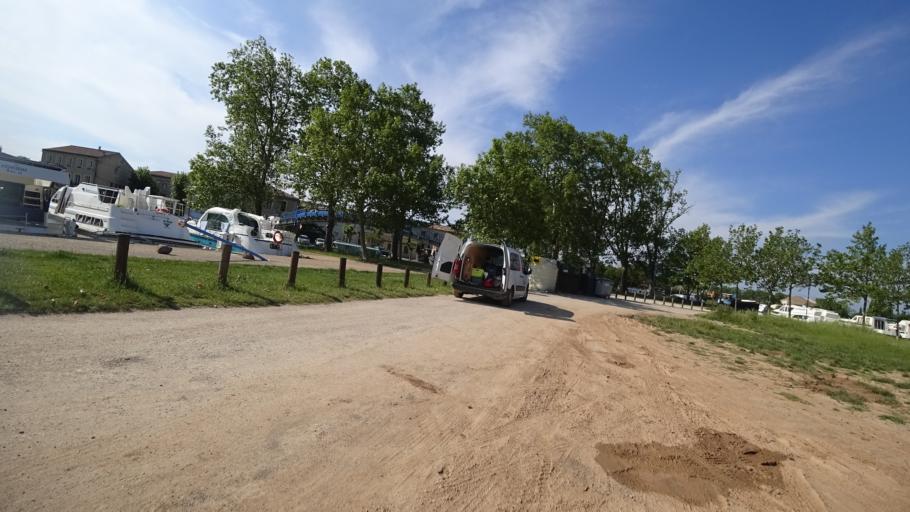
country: FR
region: Languedoc-Roussillon
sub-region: Departement de l'Herault
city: Olonzac
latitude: 43.2687
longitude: 2.7169
